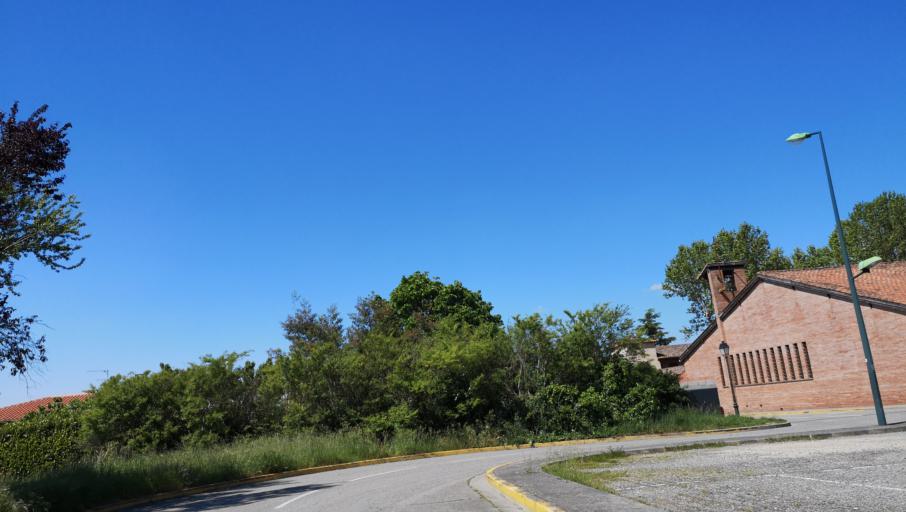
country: FR
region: Midi-Pyrenees
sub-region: Departement de la Haute-Garonne
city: Beauzelle
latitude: 43.6796
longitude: 1.3670
